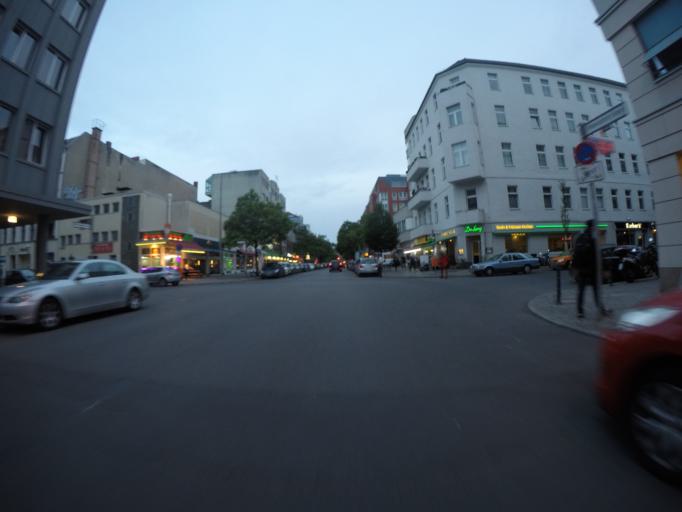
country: DE
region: Berlin
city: Charlottenburg-Nord
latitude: 52.5139
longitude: 13.3049
